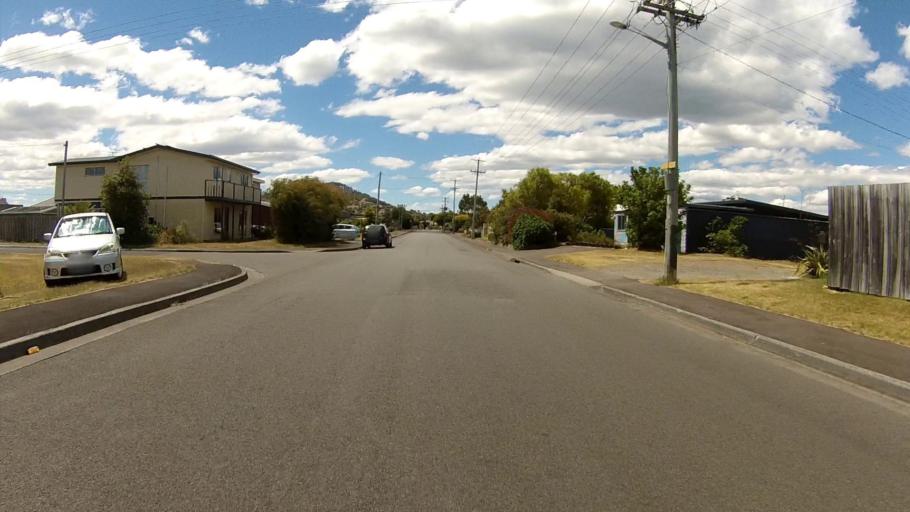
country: AU
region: Tasmania
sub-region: Clarence
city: Lauderdale
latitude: -42.8992
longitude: 147.4954
